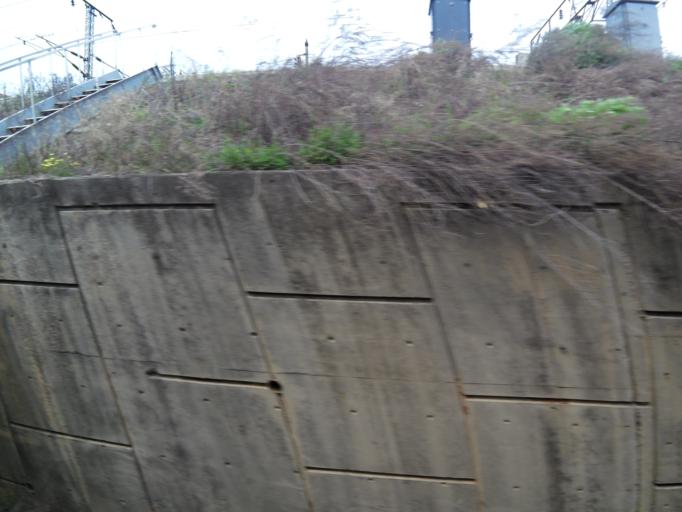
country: KR
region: Gyeonggi-do
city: Kwangmyong
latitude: 37.5133
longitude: 126.9247
